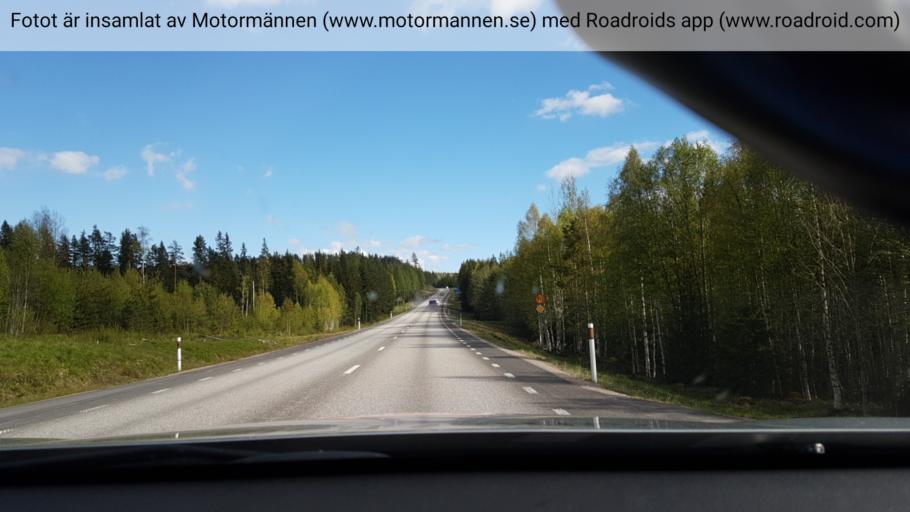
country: SE
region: Dalarna
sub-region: Rattviks Kommun
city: Raettvik
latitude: 60.7937
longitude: 15.2759
